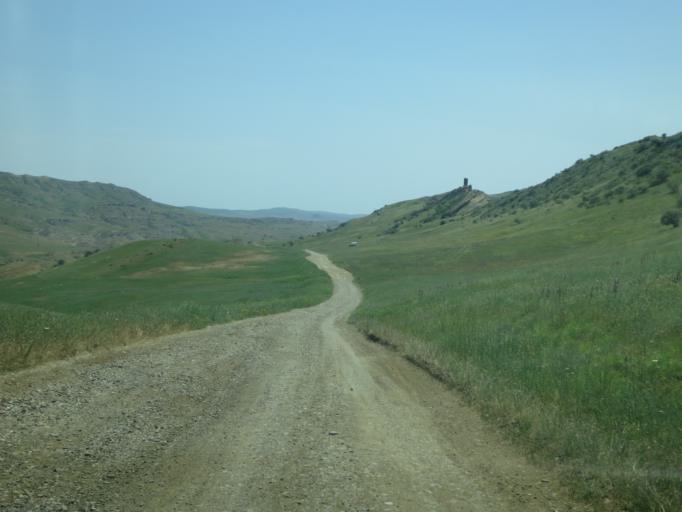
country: AZ
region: Agstafa
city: Saloglu
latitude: 41.4624
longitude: 45.3407
